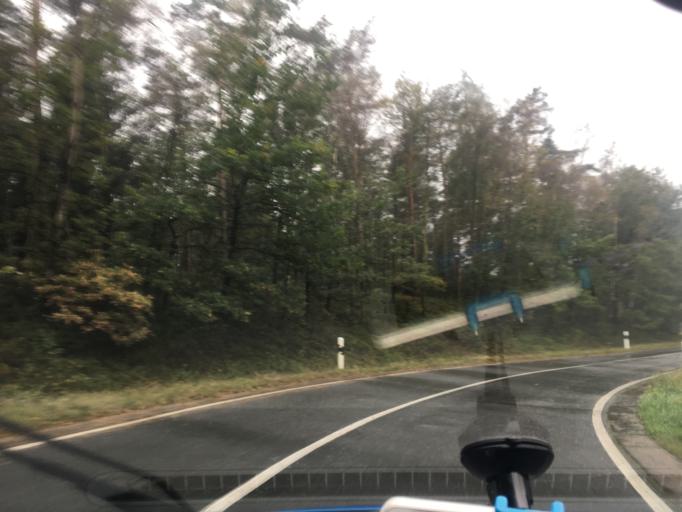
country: DE
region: Lower Saxony
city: Bispingen
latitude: 53.0612
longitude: 9.9952
